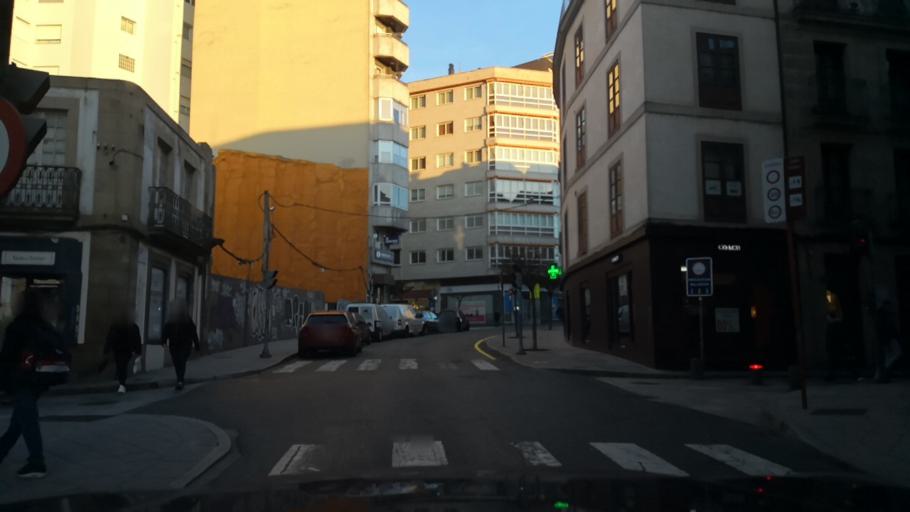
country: ES
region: Galicia
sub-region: Provincia de Ourense
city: Ourense
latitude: 42.3392
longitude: -7.8634
